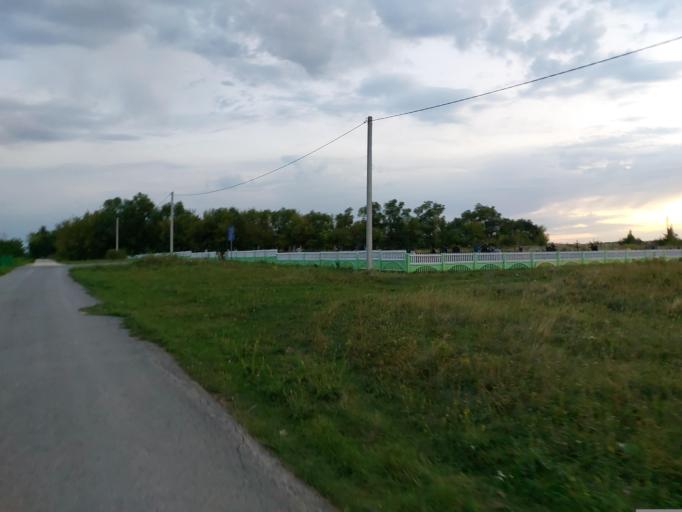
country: RU
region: Lipetsk
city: Dolgorukovo
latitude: 52.3788
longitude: 38.0456
